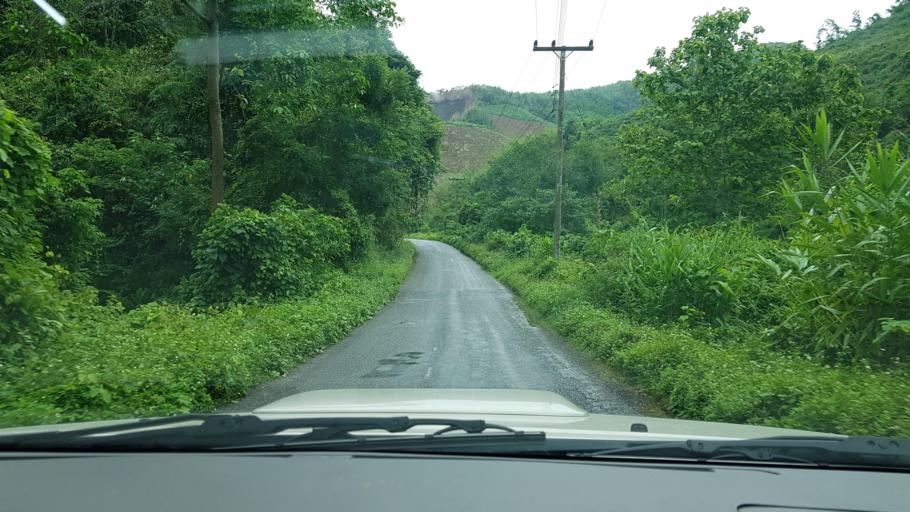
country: LA
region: Phongsali
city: Khoa
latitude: 21.1026
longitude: 102.2892
